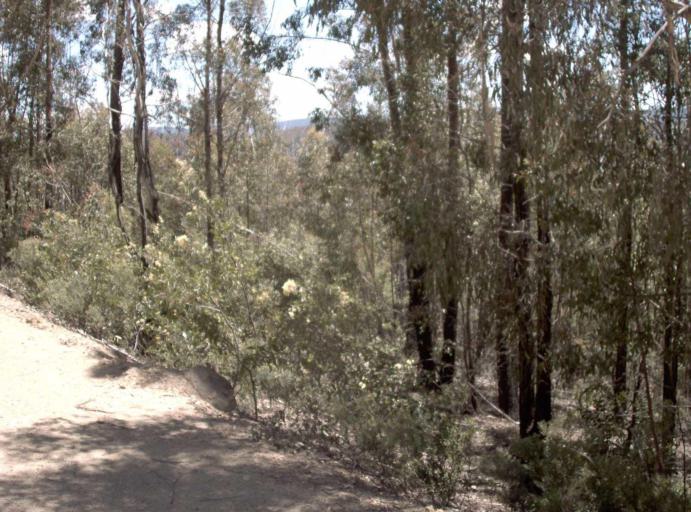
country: AU
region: New South Wales
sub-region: Snowy River
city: Jindabyne
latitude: -37.0810
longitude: 148.3297
